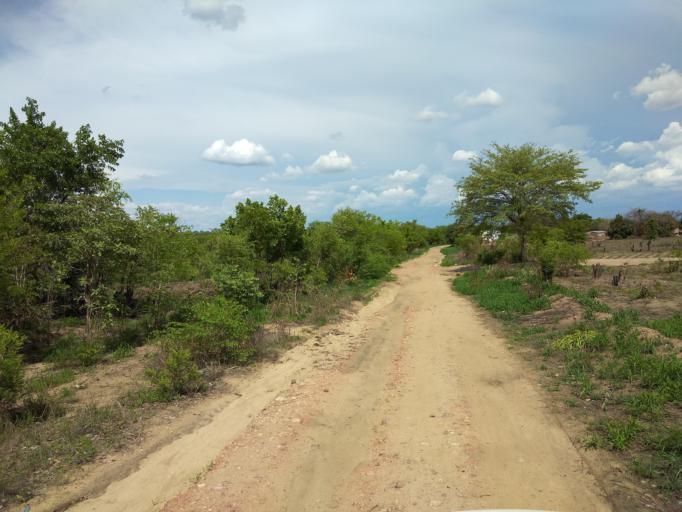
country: ZM
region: Eastern
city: Nyimba
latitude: -14.1175
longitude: 30.1357
